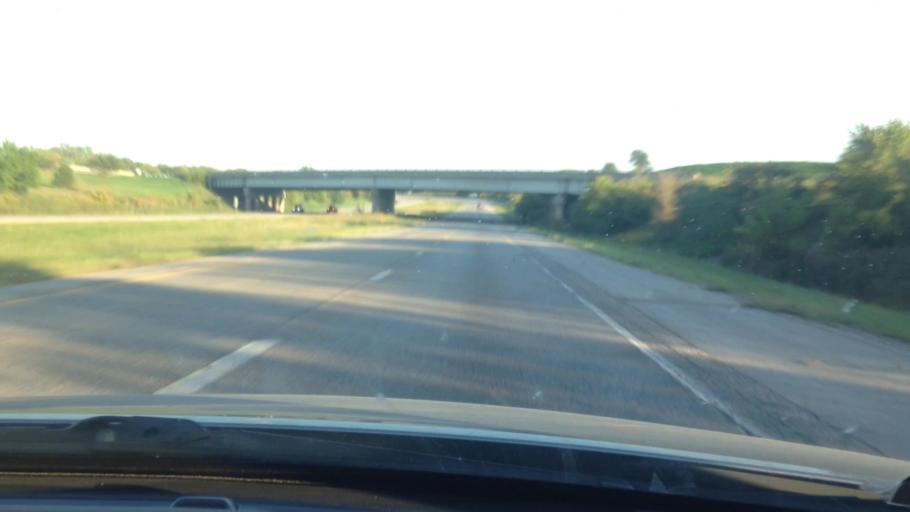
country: US
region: Missouri
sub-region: Platte County
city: Weatherby Lake
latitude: 39.3119
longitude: -94.6738
